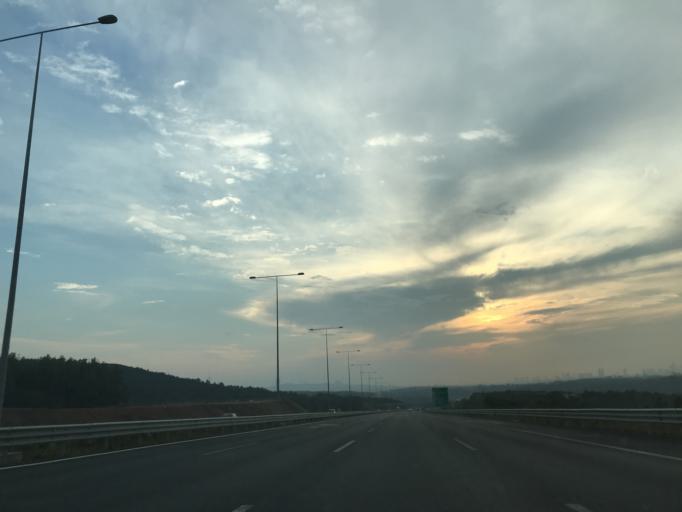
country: TR
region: Istanbul
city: Umraniye
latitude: 41.0503
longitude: 29.1540
